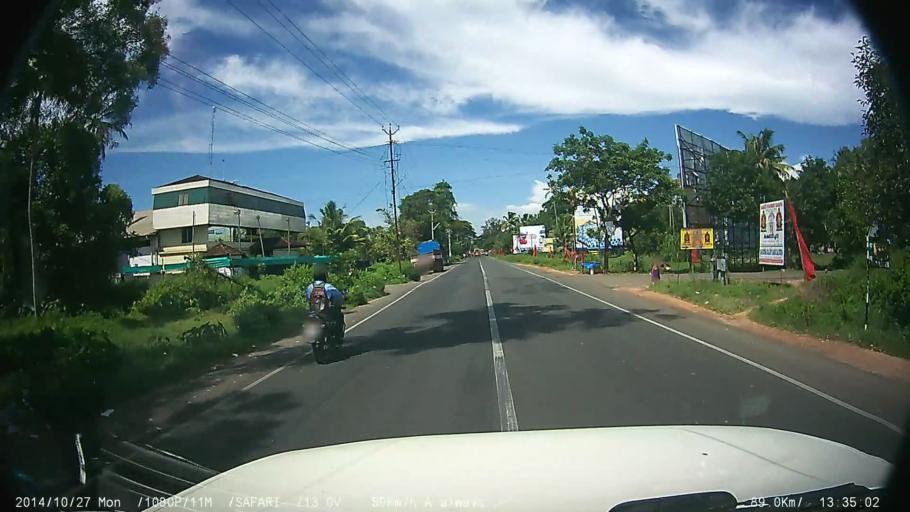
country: IN
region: Kerala
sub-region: Alappuzha
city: Shertallai
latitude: 9.5898
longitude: 76.3278
